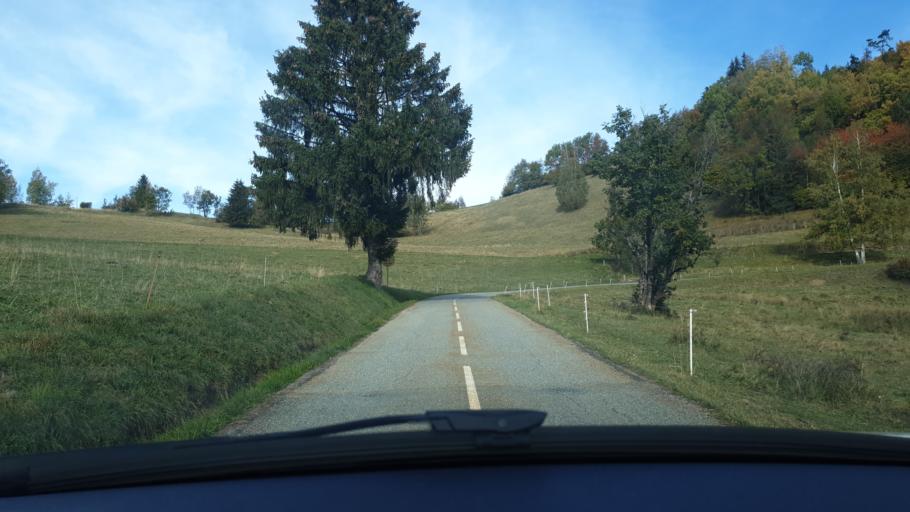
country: FR
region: Rhone-Alpes
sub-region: Departement de la Savoie
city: Aiton
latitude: 45.5026
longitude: 6.2220
